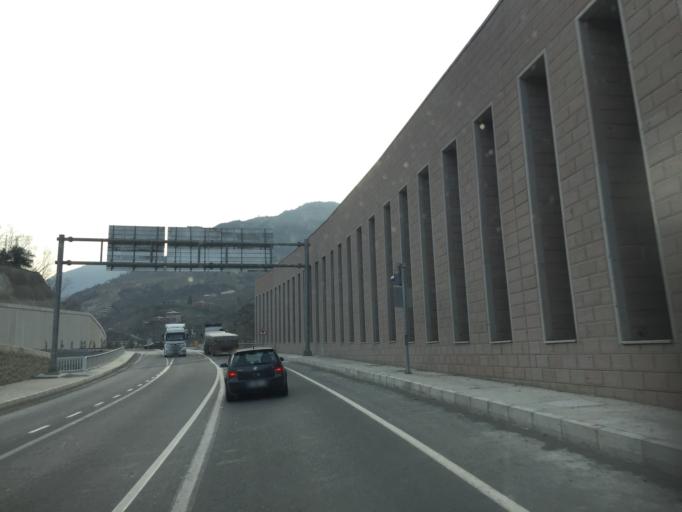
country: TR
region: Trabzon
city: Macka
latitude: 40.8037
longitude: 39.5888
